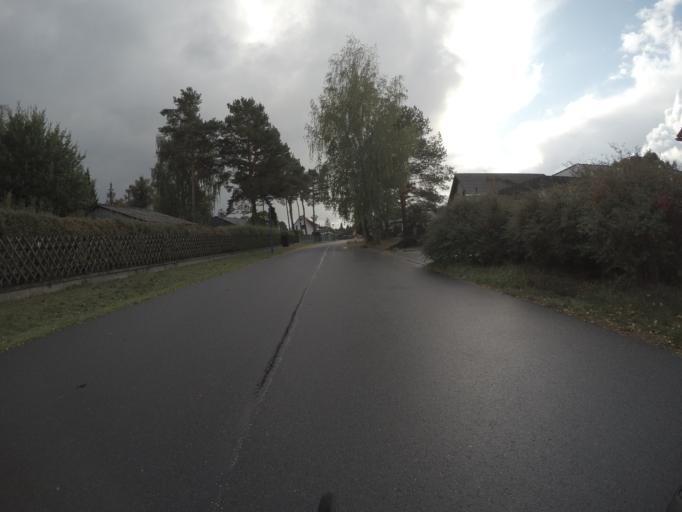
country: DE
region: Brandenburg
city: Wandlitz
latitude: 52.7102
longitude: 13.4349
